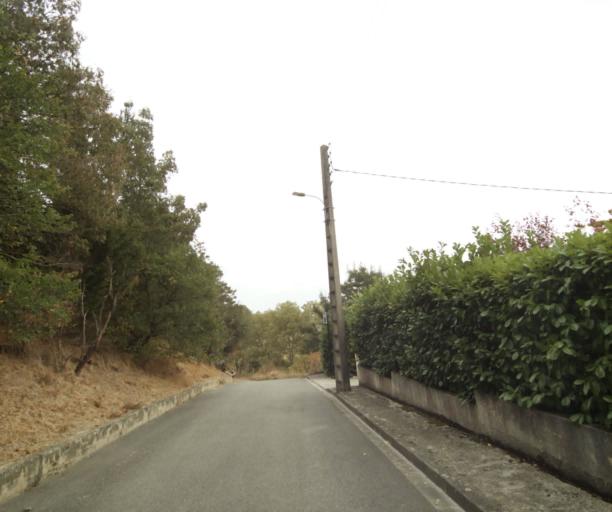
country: FR
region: Midi-Pyrenees
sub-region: Departement de la Haute-Garonne
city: Villefranche-de-Lauragais
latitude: 43.4019
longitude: 1.7255
